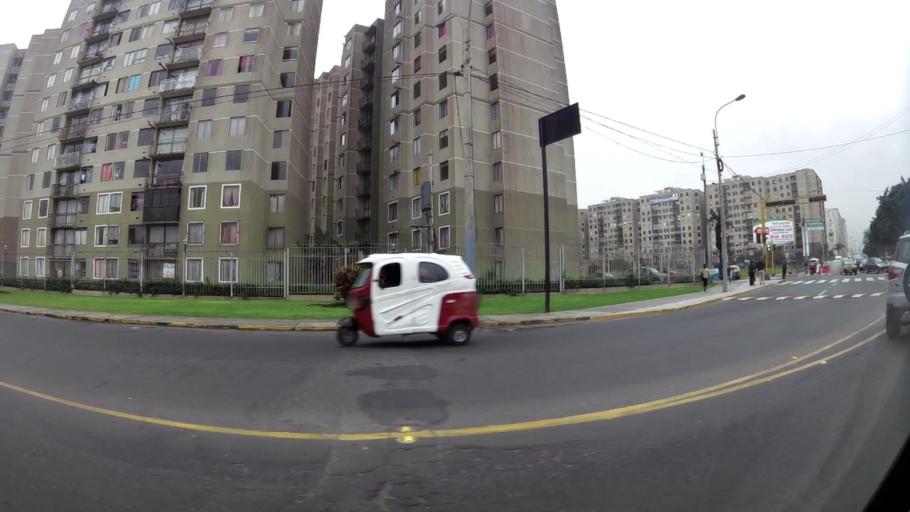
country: PE
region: Callao
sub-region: Callao
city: Callao
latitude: -12.0844
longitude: -77.0901
